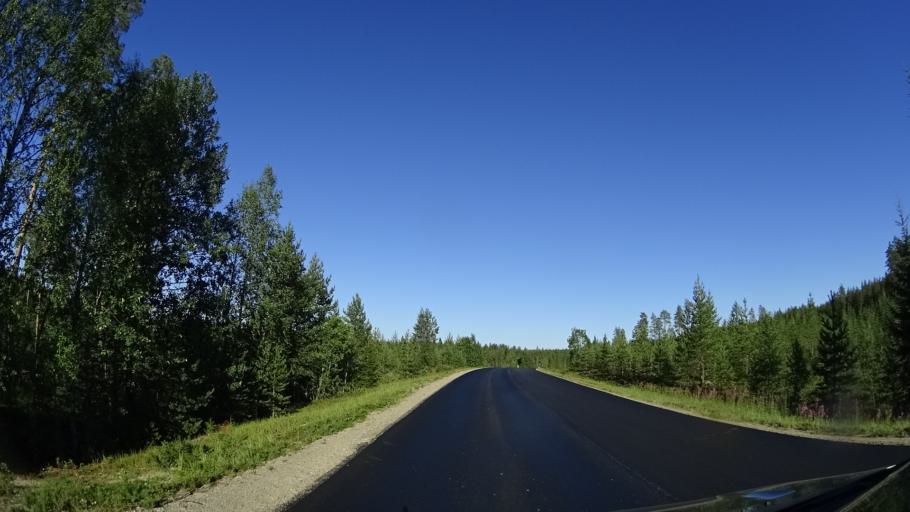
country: FI
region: North Karelia
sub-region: Pielisen Karjala
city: Valtimo
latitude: 63.5600
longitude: 28.6114
